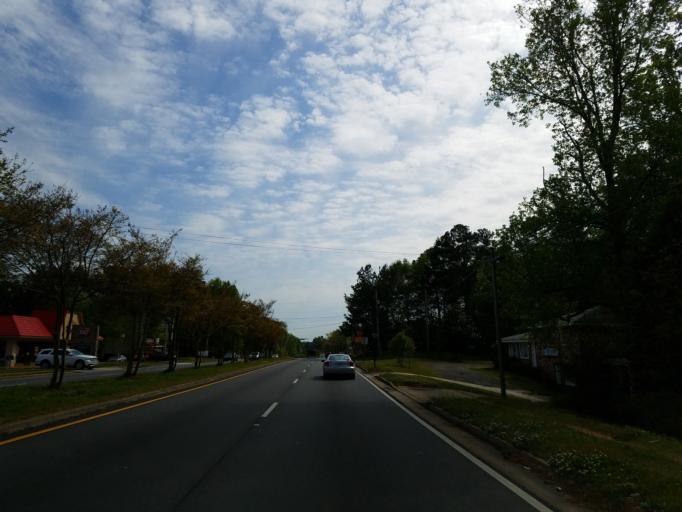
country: US
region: Georgia
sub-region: Cobb County
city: Austell
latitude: 33.8299
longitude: -84.6135
